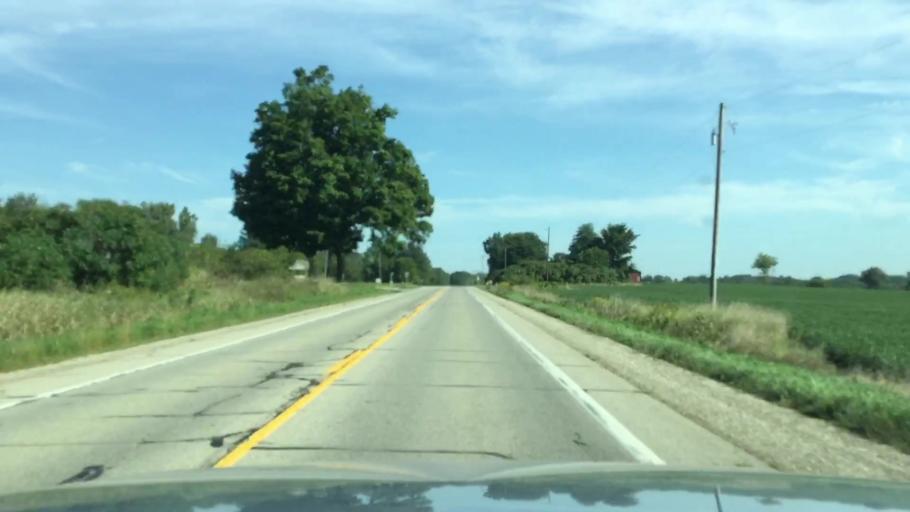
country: US
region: Michigan
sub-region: Lenawee County
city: Manitou Beach-Devils Lake
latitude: 41.9547
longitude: -84.3671
